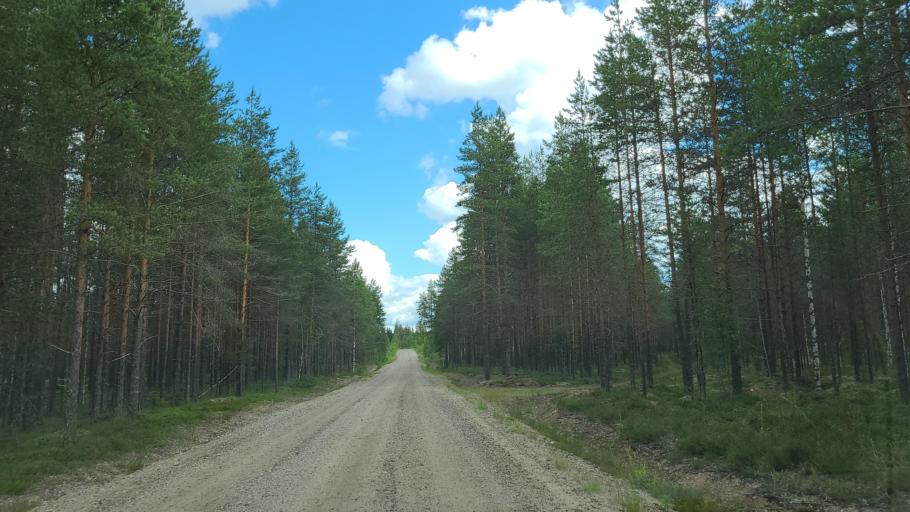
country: FI
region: Northern Savo
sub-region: Koillis-Savo
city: Kaavi
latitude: 63.0435
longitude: 28.8132
